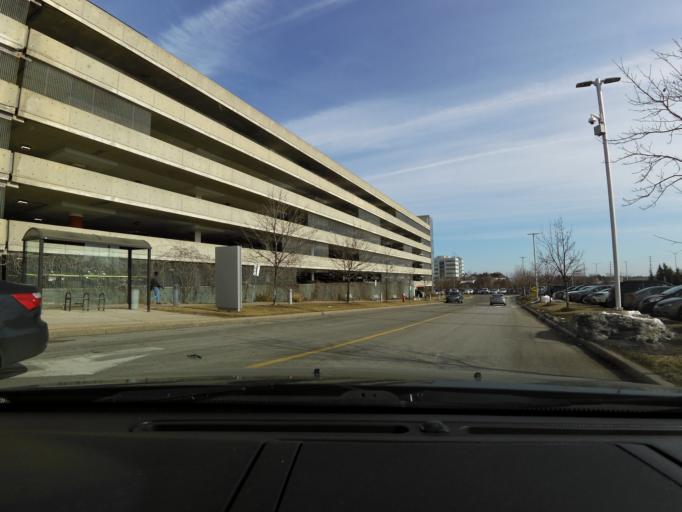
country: CA
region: Ontario
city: Brampton
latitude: 43.7478
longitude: -79.7417
